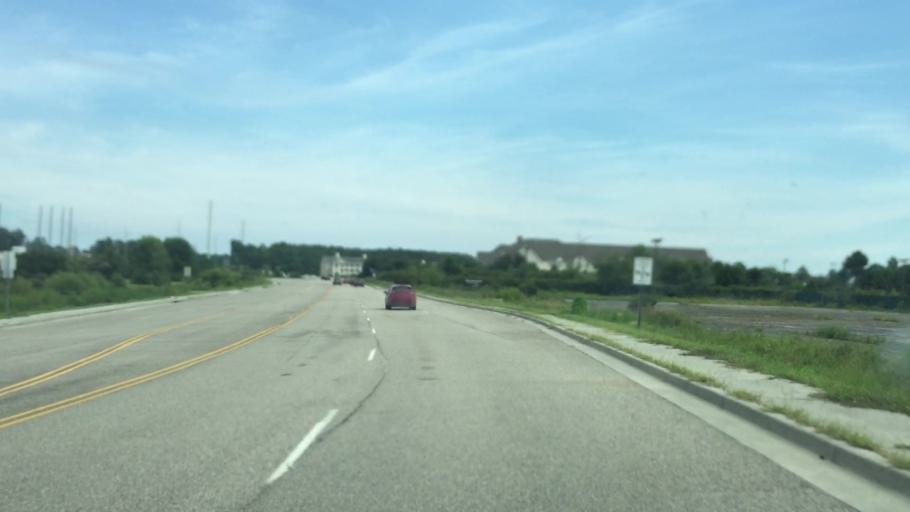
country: US
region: South Carolina
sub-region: Horry County
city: Forestbrook
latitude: 33.7163
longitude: -78.9306
